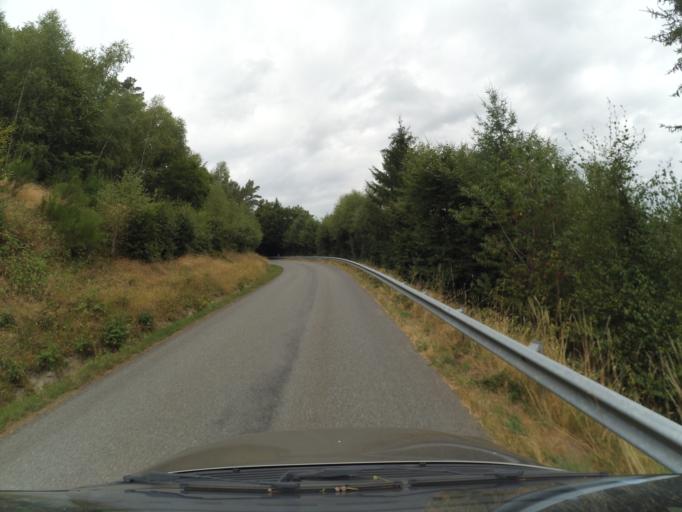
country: FR
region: Limousin
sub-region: Departement de la Correze
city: Meymac
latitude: 45.6653
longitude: 2.1265
